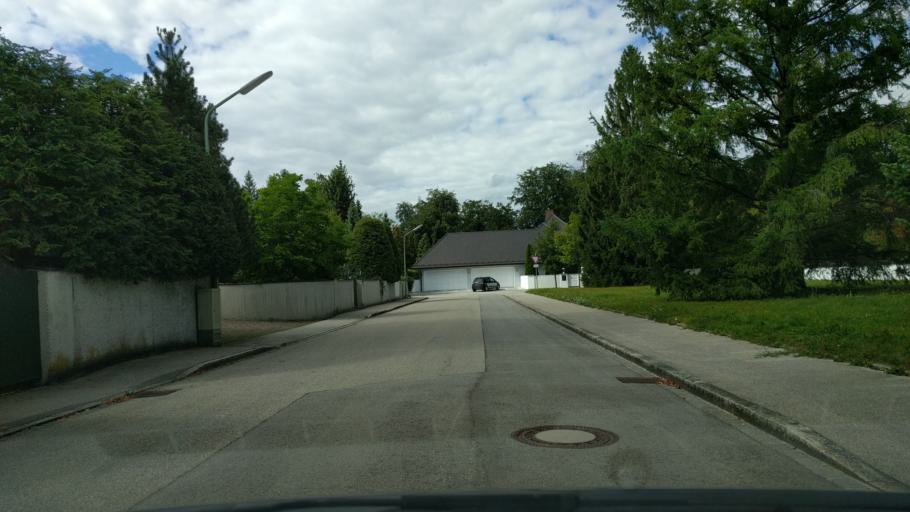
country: DE
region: Bavaria
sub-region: Upper Bavaria
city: Pullach im Isartal
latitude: 48.0551
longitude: 11.5429
